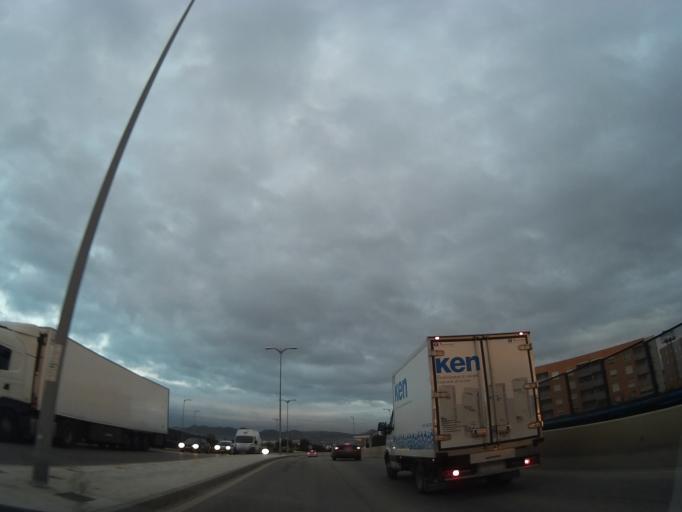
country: ES
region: Andalusia
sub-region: Provincia de Malaga
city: Malaga
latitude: 36.7025
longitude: -4.4923
